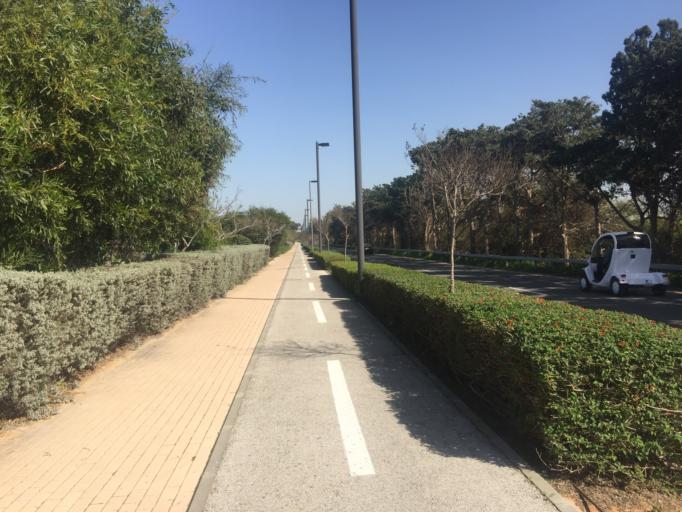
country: IL
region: Haifa
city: Qesarya
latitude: 32.5017
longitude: 34.8957
